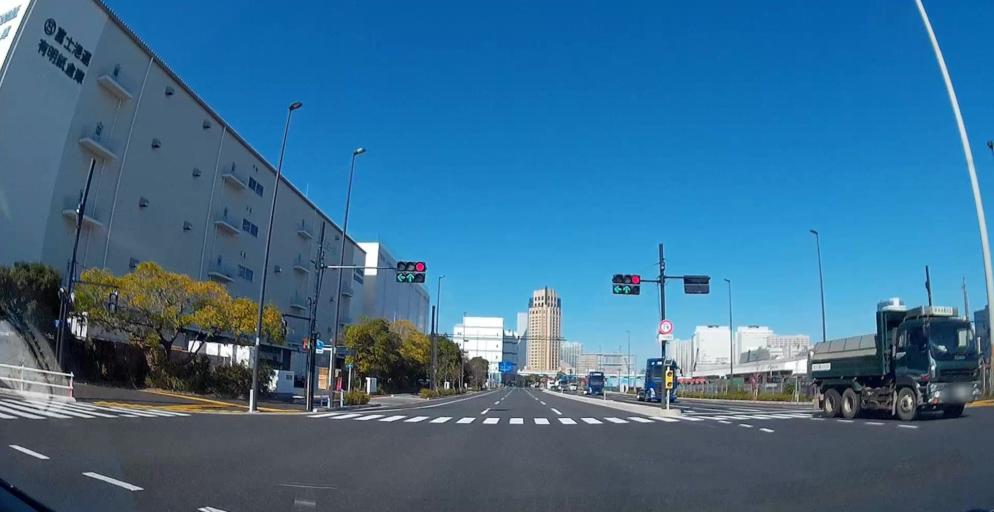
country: JP
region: Tokyo
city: Urayasu
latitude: 35.6238
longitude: 139.7912
